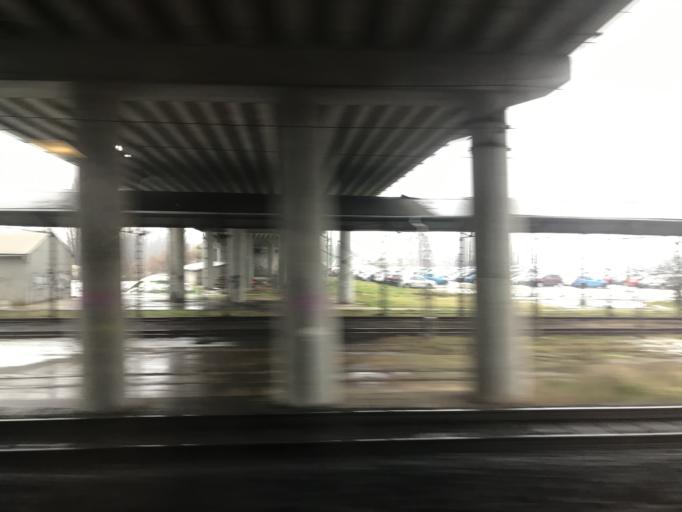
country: HU
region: Gyor-Moson-Sopron
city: Gyor
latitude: 47.6784
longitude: 17.6247
